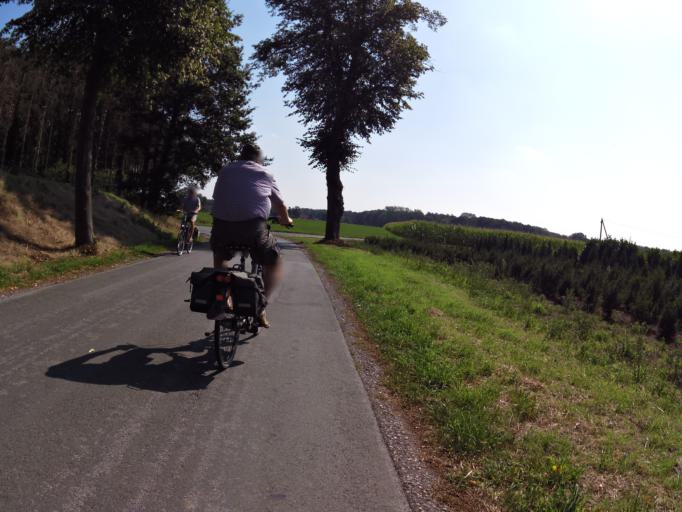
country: DE
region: North Rhine-Westphalia
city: Stadtlohn
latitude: 51.9993
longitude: 6.9485
